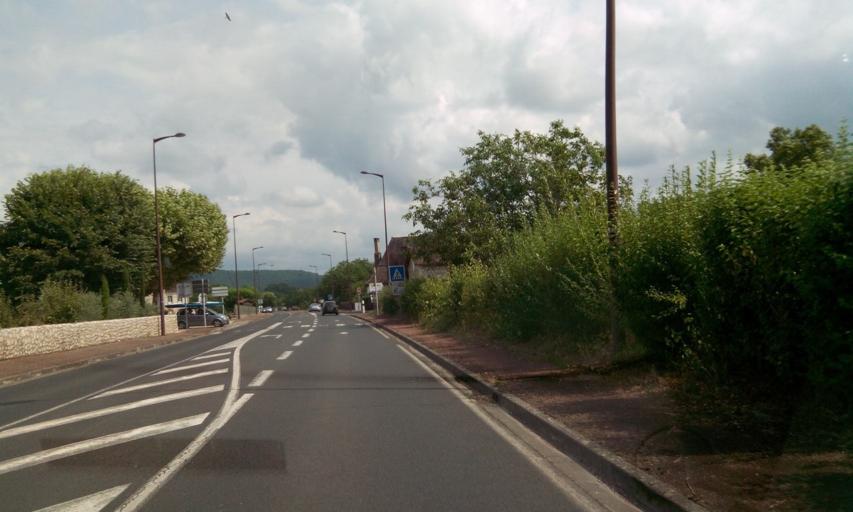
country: FR
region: Midi-Pyrenees
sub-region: Departement du Lot
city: Souillac
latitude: 44.8866
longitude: 1.4067
